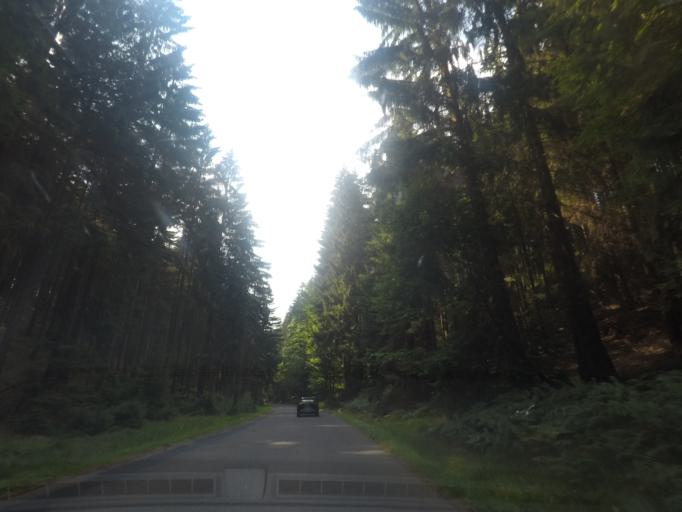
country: DE
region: Saxony
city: Sebnitz
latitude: 50.8761
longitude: 14.2894
